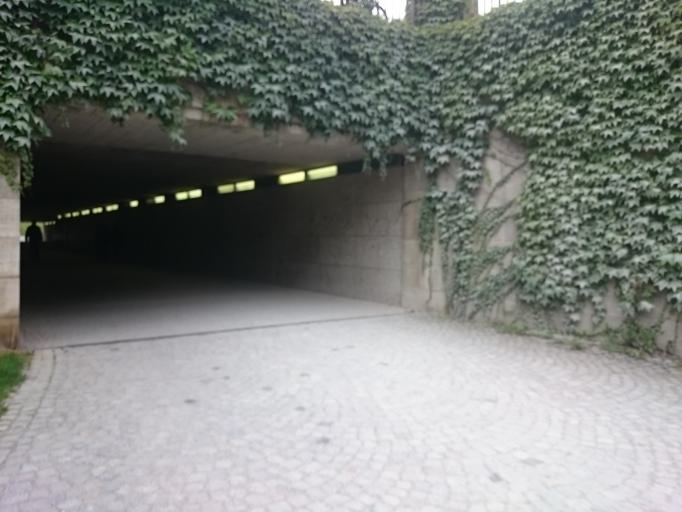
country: DE
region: Bavaria
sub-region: Upper Bavaria
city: Munich
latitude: 48.1446
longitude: 11.5839
